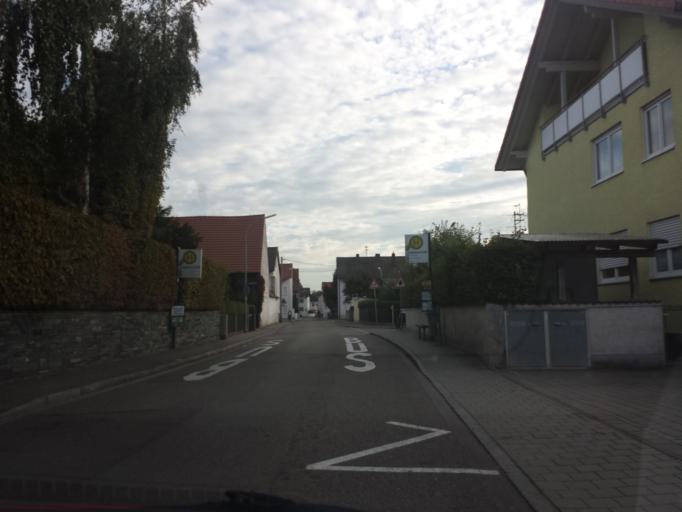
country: DE
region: Bavaria
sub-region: Upper Bavaria
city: Weichering
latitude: 48.7559
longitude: 11.3447
